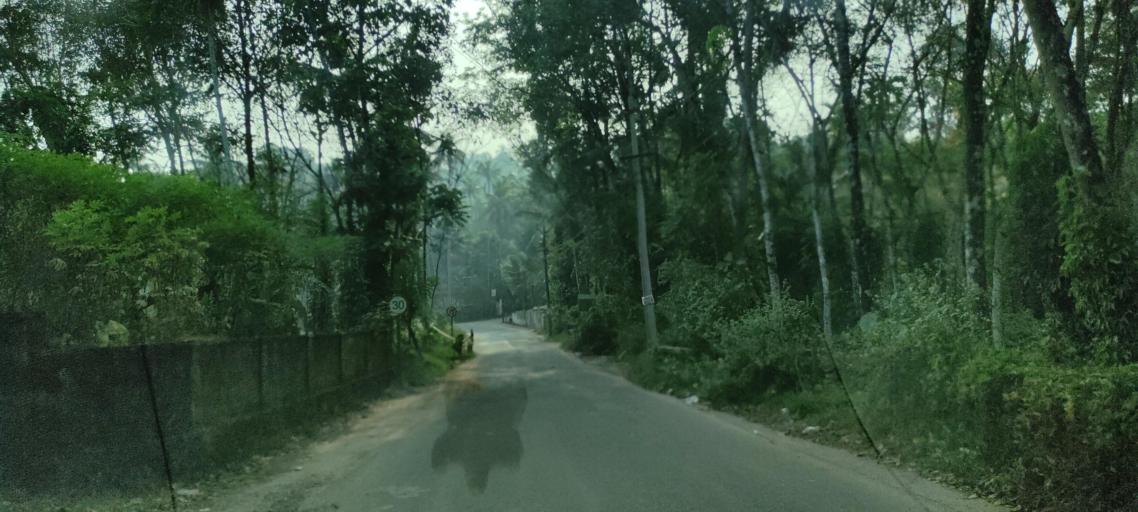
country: IN
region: Kerala
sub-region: Ernakulam
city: Piravam
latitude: 9.7750
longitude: 76.4929
